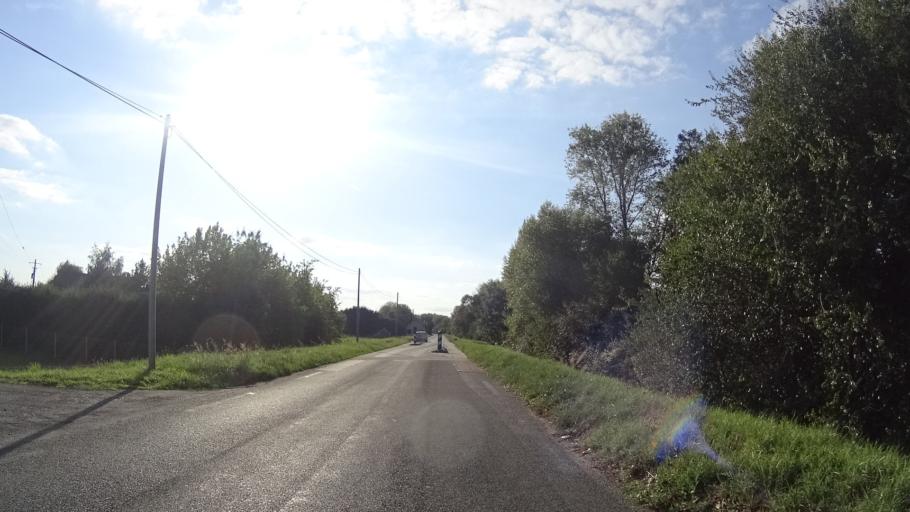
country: FR
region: Pays de la Loire
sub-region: Departement de Maine-et-Loire
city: Ingrandes
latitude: 47.4002
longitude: -0.9073
